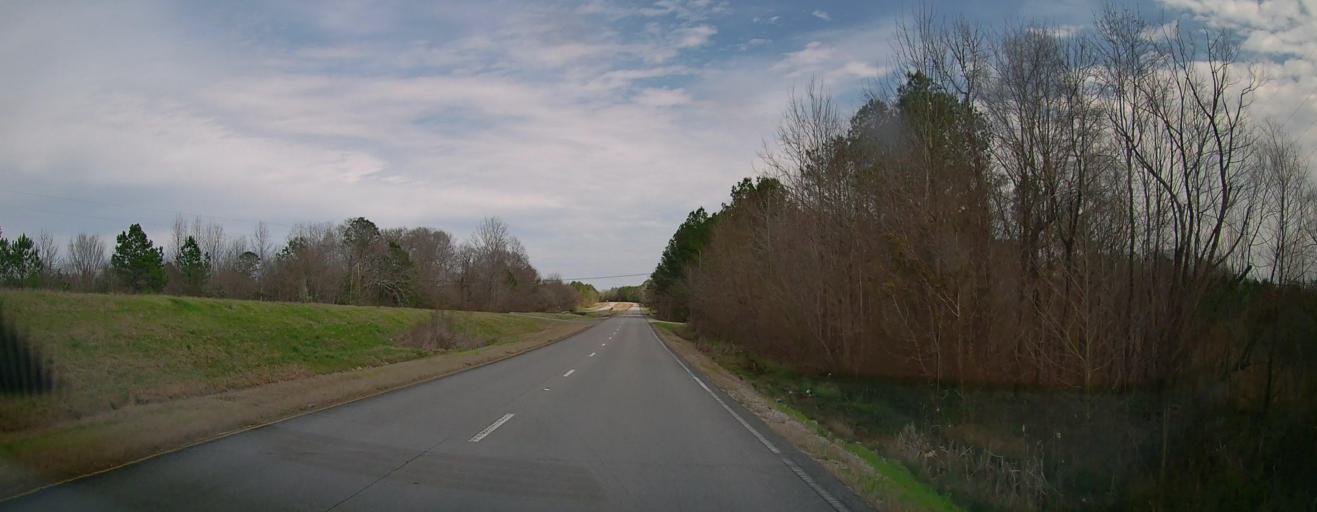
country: US
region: Alabama
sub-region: Marion County
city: Winfield
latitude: 33.9300
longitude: -87.6830
